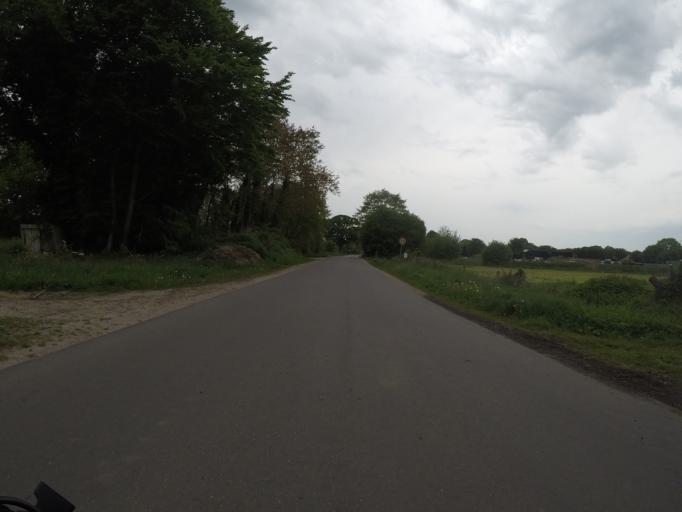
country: DE
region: Schleswig-Holstein
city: Kisdorf
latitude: 53.7829
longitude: 10.0198
